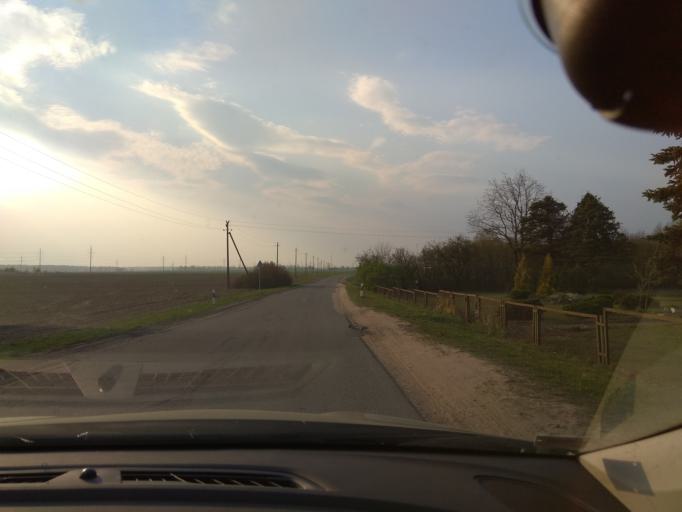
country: LT
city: Baltoji Voke
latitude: 54.5999
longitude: 25.1397
